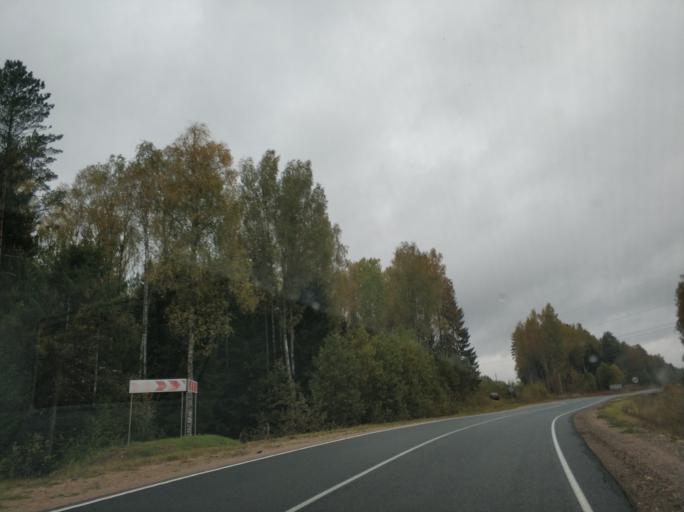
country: RU
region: Pskov
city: Opochka
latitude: 56.5202
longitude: 28.6562
